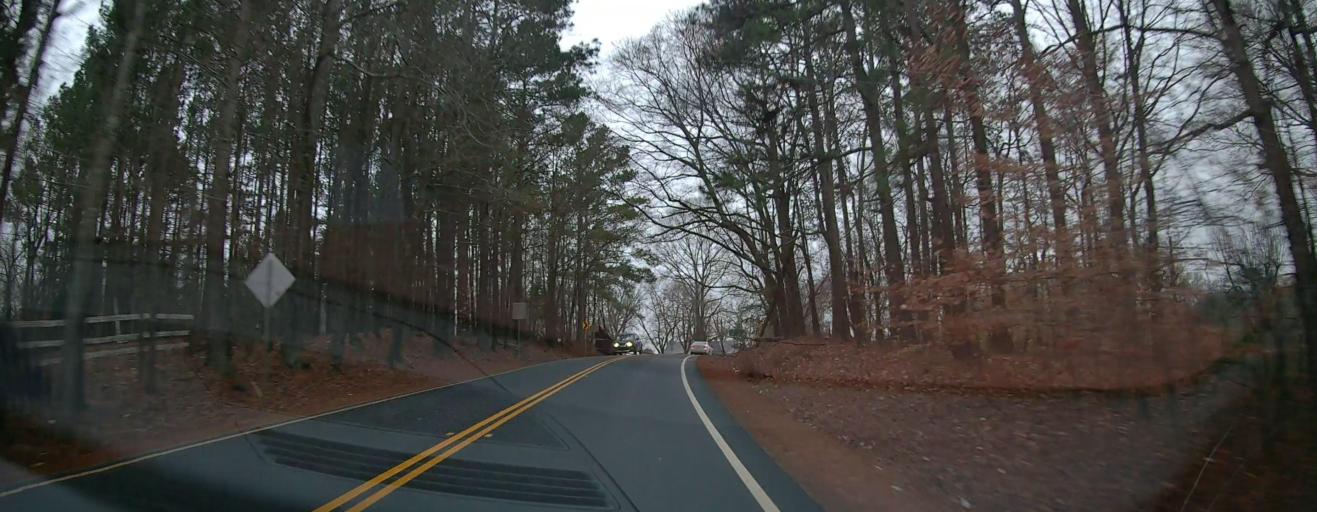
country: US
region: Georgia
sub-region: Lamar County
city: Barnesville
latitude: 33.0641
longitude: -84.2481
